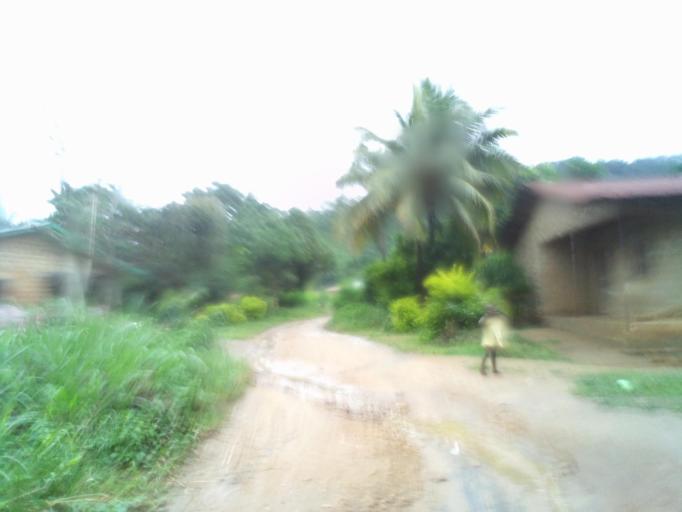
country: SL
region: Eastern Province
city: Kenema
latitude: 7.8533
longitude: -11.2117
